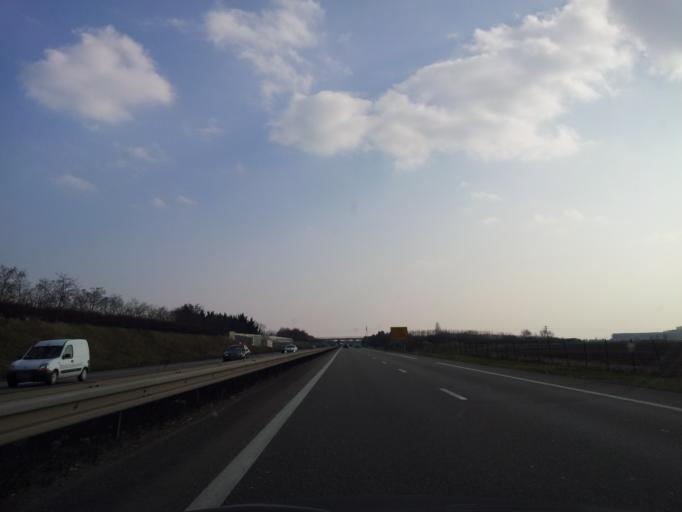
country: FR
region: Alsace
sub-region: Departement du Haut-Rhin
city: Sainte-Croix-en-Plaine
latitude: 48.0080
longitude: 7.3771
